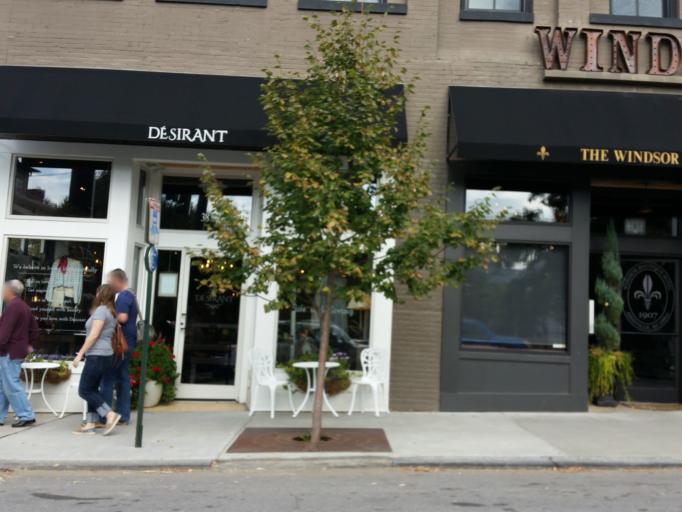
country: US
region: North Carolina
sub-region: Buncombe County
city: Asheville
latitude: 35.5965
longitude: -82.5520
